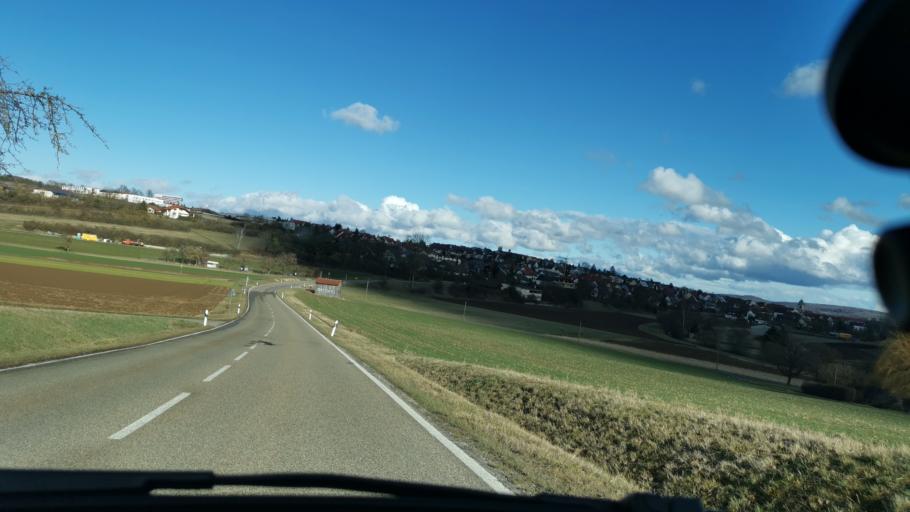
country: DE
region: Baden-Wuerttemberg
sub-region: Regierungsbezirk Stuttgart
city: Weil der Stadt
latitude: 48.7780
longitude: 8.8903
